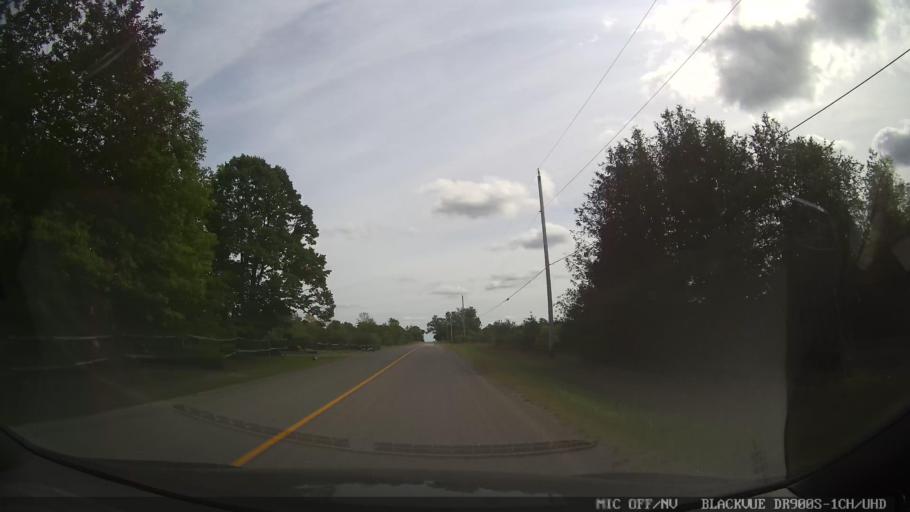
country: CA
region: Ontario
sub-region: Lanark County
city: Smiths Falls
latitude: 44.8862
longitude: -75.9173
